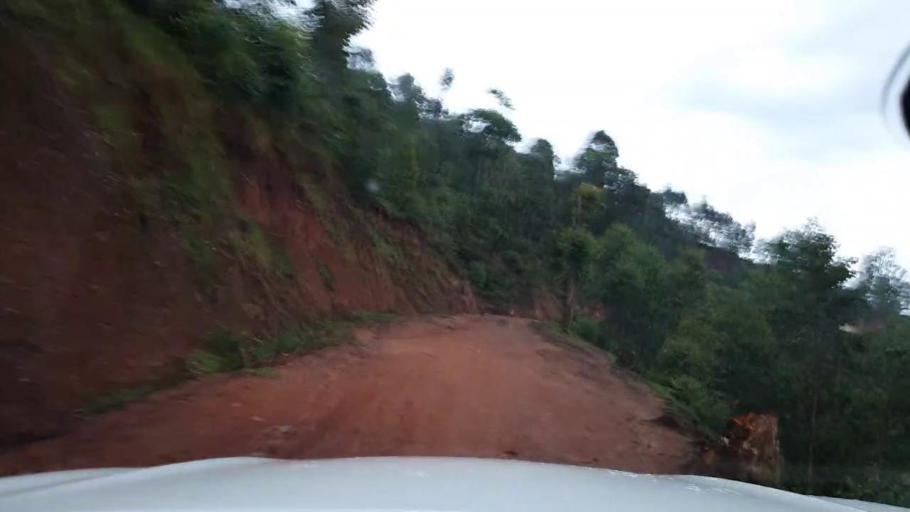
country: BI
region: Kayanza
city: Kayanza
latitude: -2.7189
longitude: 29.5443
